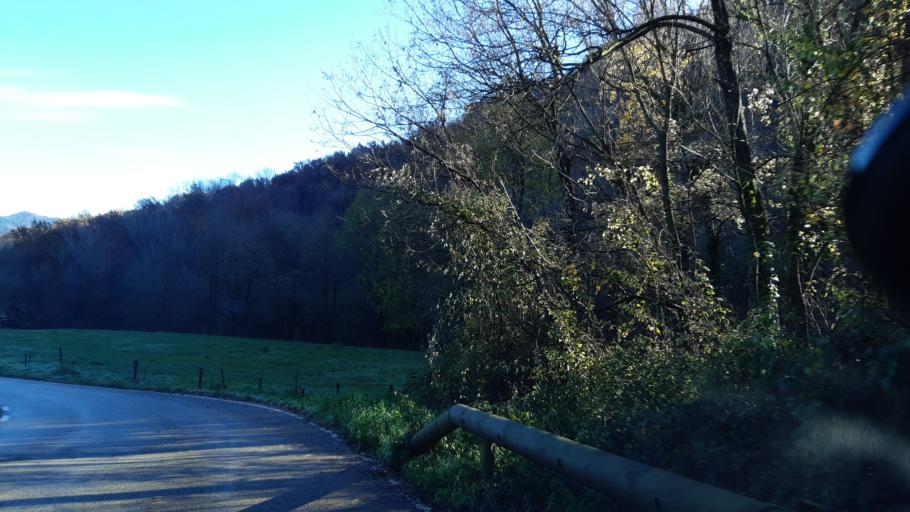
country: ES
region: Catalonia
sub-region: Provincia de Girona
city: Bas
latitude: 42.1492
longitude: 2.4107
